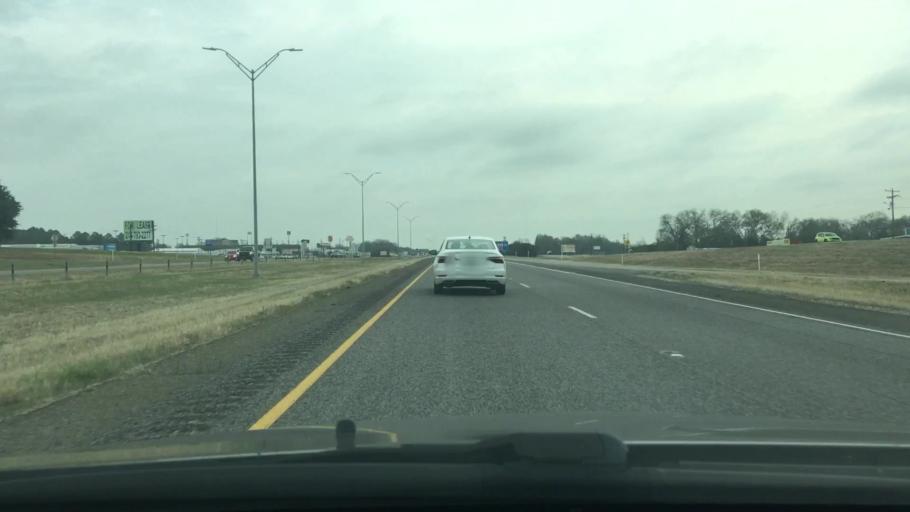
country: US
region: Texas
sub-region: Freestone County
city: Fairfield
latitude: 31.7255
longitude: -96.1801
